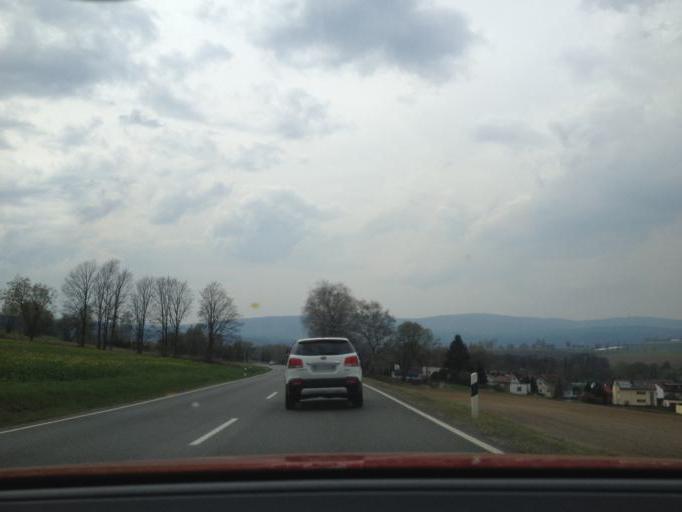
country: DE
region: Bavaria
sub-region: Upper Franconia
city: Trostau
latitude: 50.0180
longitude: 11.9703
